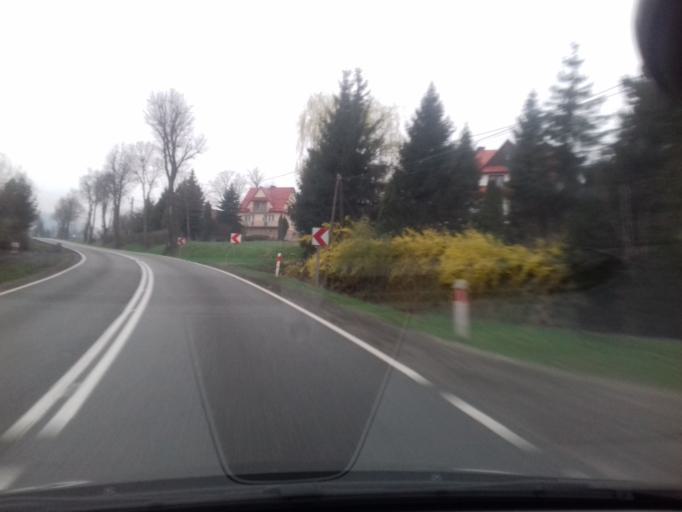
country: PL
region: Lesser Poland Voivodeship
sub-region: Powiat limanowski
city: Tymbark
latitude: 49.7234
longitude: 20.3308
